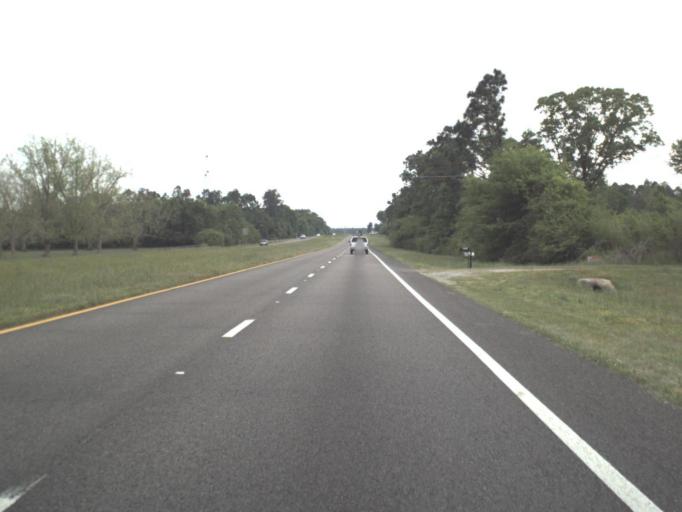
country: US
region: Florida
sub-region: Escambia County
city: Molino
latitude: 30.6736
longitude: -87.3513
